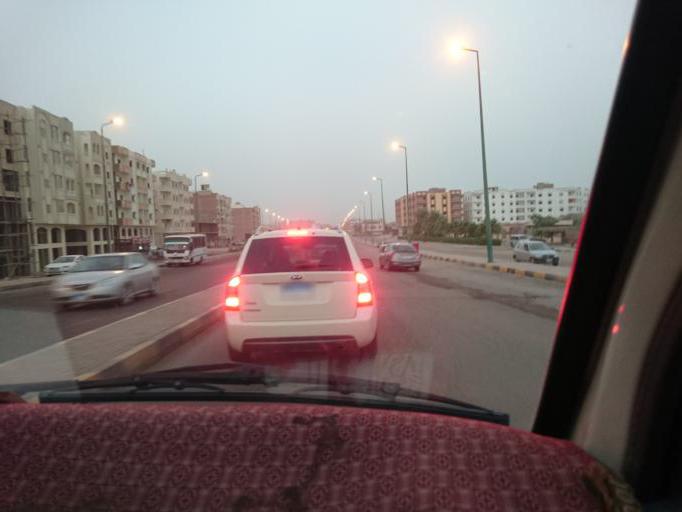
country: EG
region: Red Sea
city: Hurghada
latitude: 27.2241
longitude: 33.8275
